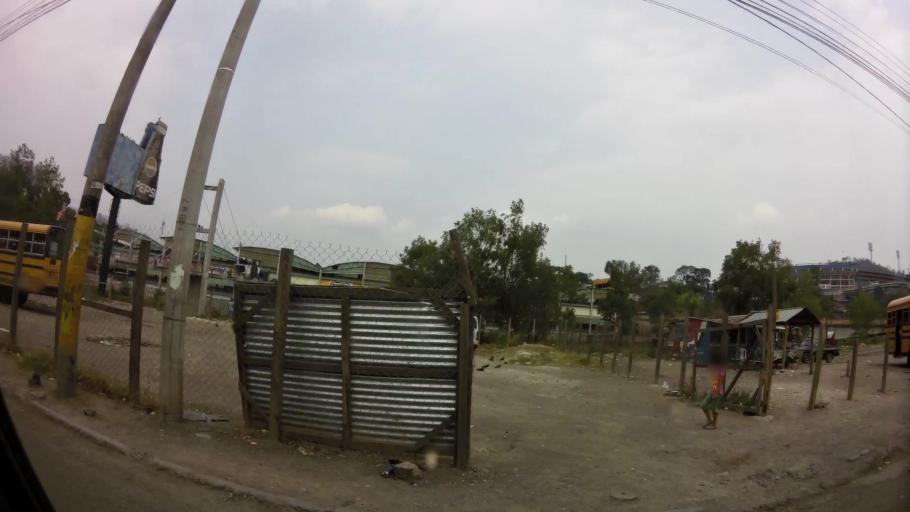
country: HN
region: Francisco Morazan
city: Tegucigalpa
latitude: 14.1016
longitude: -87.2062
